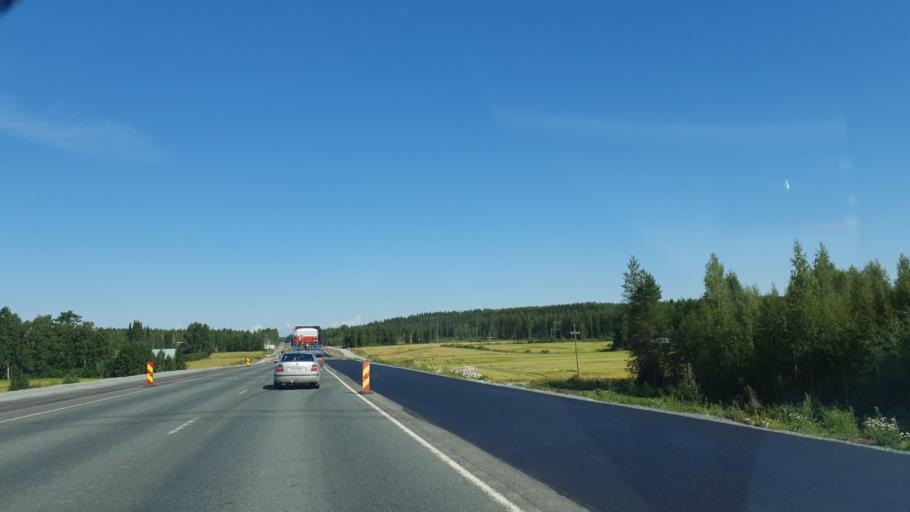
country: FI
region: Northern Savo
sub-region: Ylae-Savo
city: Lapinlahti
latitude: 63.2840
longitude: 27.4554
